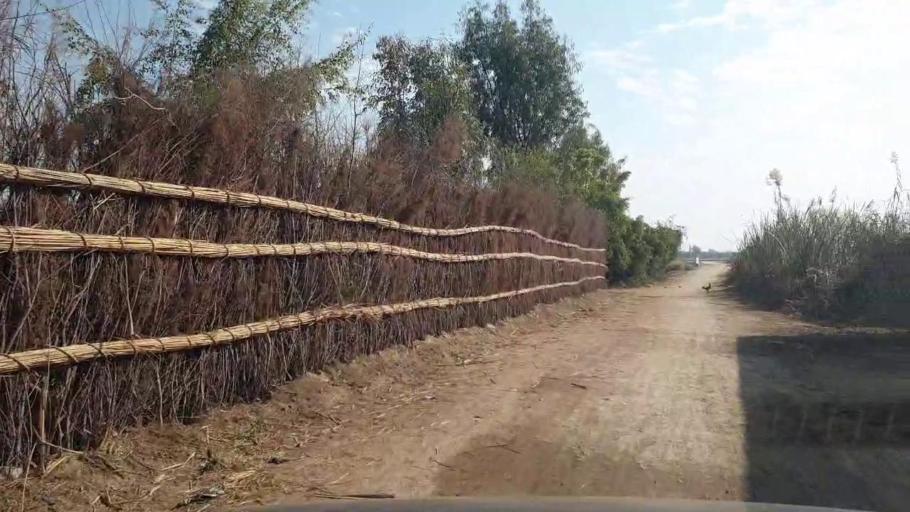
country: PK
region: Sindh
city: Hala
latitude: 25.9960
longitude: 68.4383
